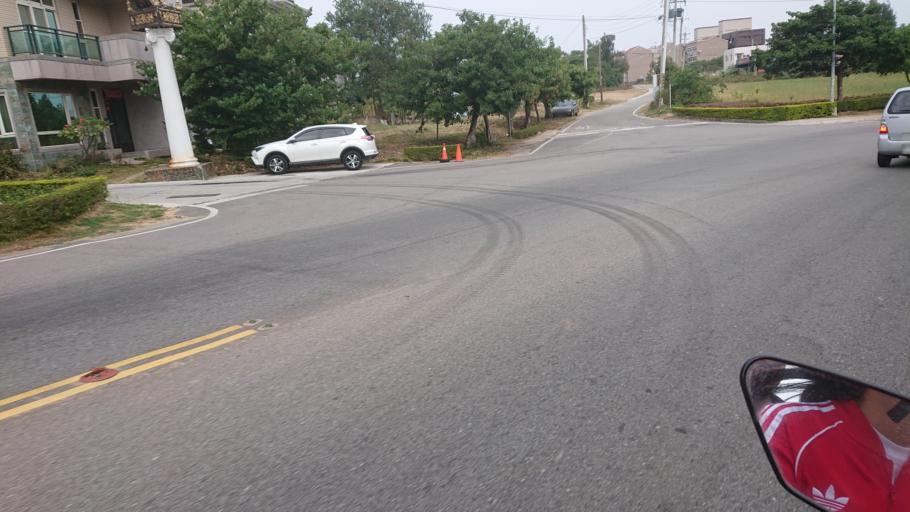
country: TW
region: Fukien
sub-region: Kinmen
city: Jincheng
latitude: 24.4211
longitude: 118.3107
